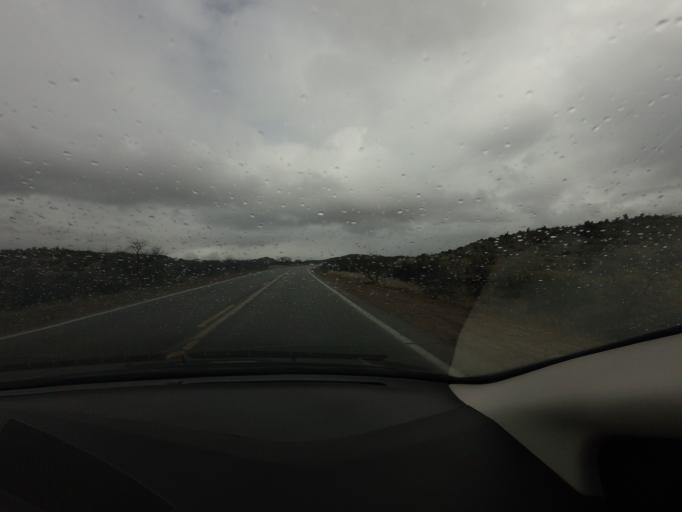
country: US
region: Arizona
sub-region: Yavapai County
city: Cornville
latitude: 34.7109
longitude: -111.8796
